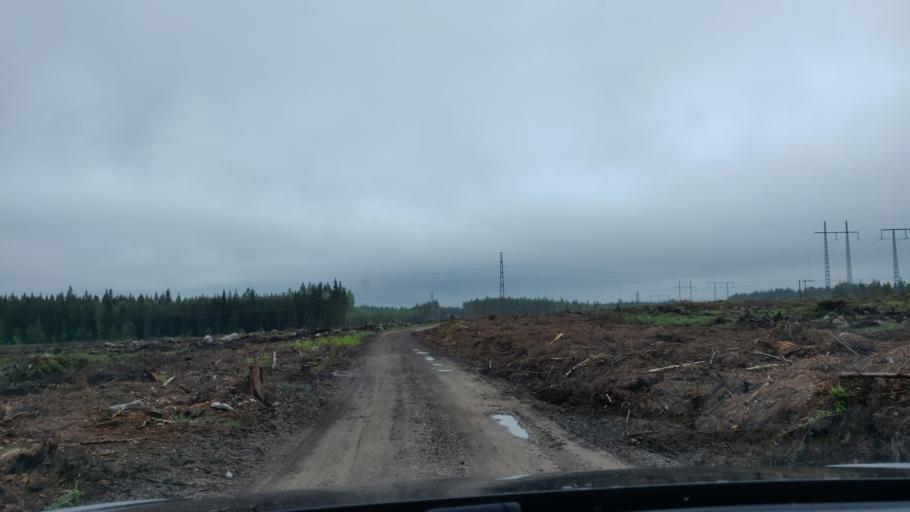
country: SE
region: Dalarna
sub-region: Avesta Kommun
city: Horndal
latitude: 60.3147
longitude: 16.4002
